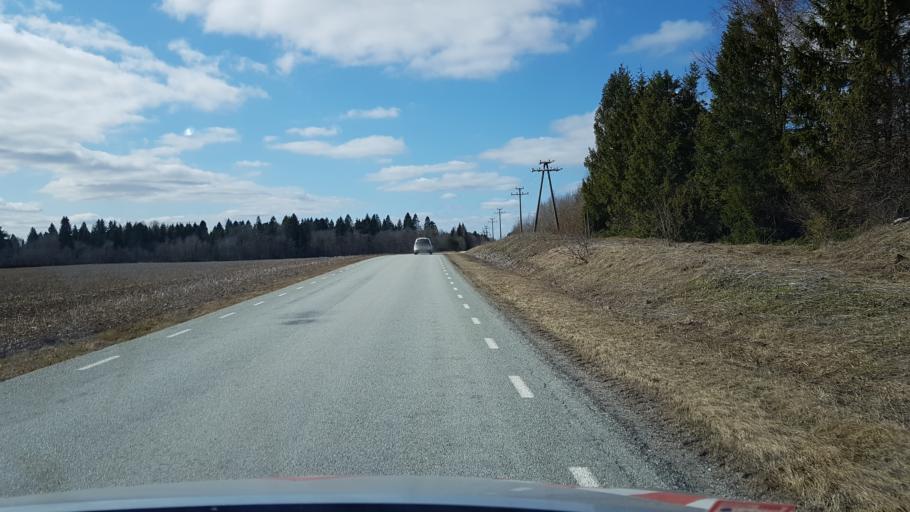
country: EE
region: Laeaene-Virumaa
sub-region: Tapa vald
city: Tapa
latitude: 59.2525
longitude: 25.8077
